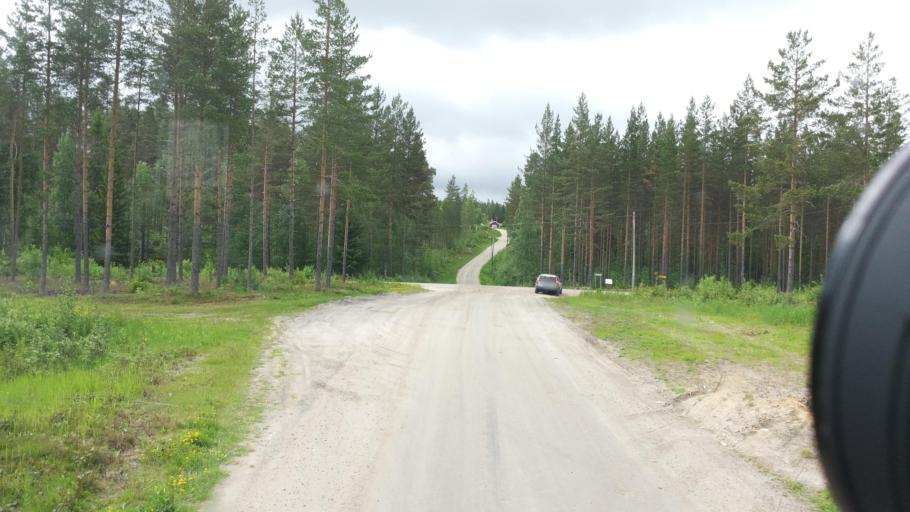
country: SE
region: Gaevleborg
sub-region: Ovanakers Kommun
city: Edsbyn
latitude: 61.5024
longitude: 15.3380
